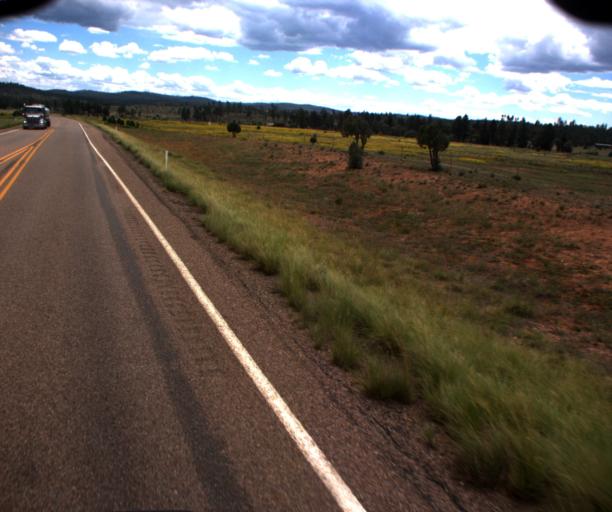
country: US
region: Arizona
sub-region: Navajo County
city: Linden
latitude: 34.3172
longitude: -110.2463
